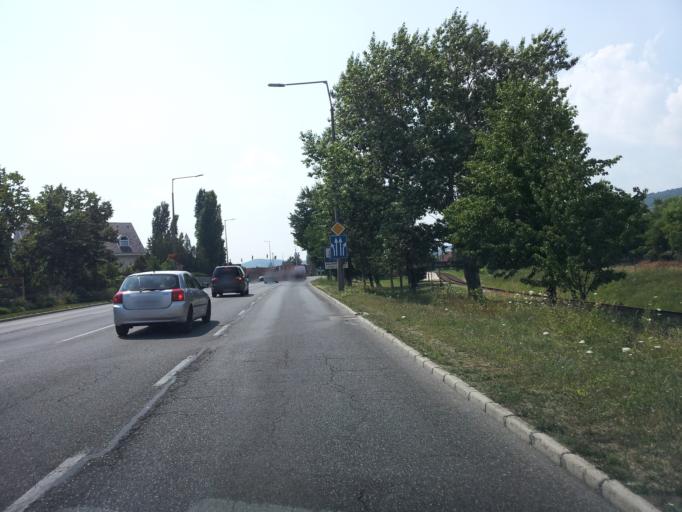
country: HU
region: Veszprem
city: Csopak
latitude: 46.9621
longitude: 17.9002
